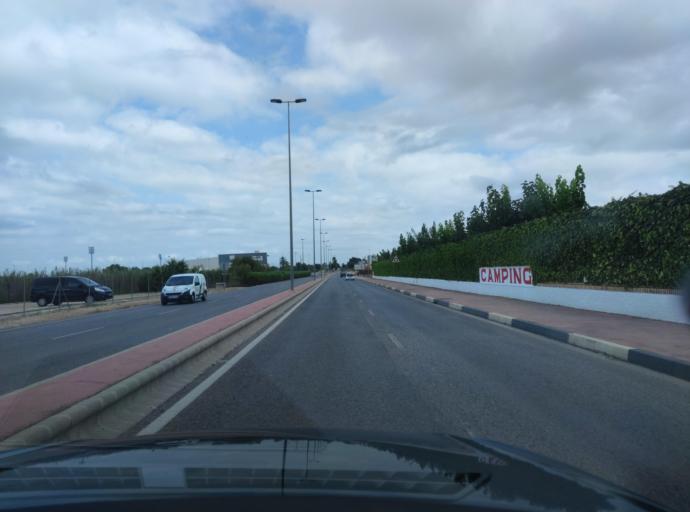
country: ES
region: Valencia
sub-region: Provincia de Alicante
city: Santa Pola
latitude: 38.2005
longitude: -0.5701
